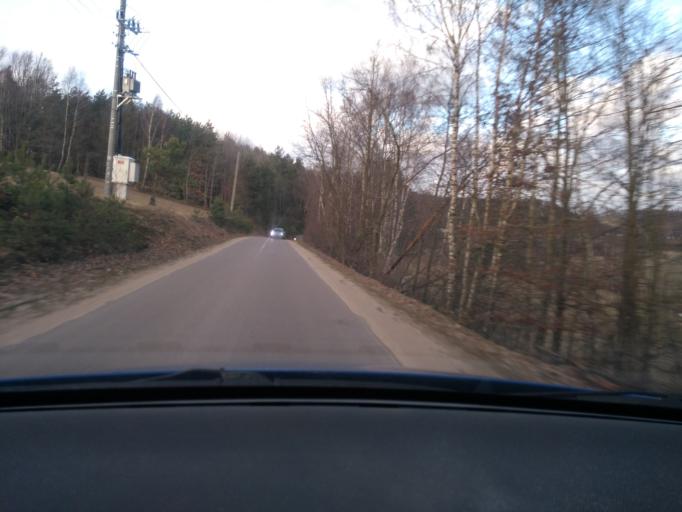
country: PL
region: Pomeranian Voivodeship
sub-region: Powiat kartuski
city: Przodkowo
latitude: 54.4136
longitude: 18.2381
